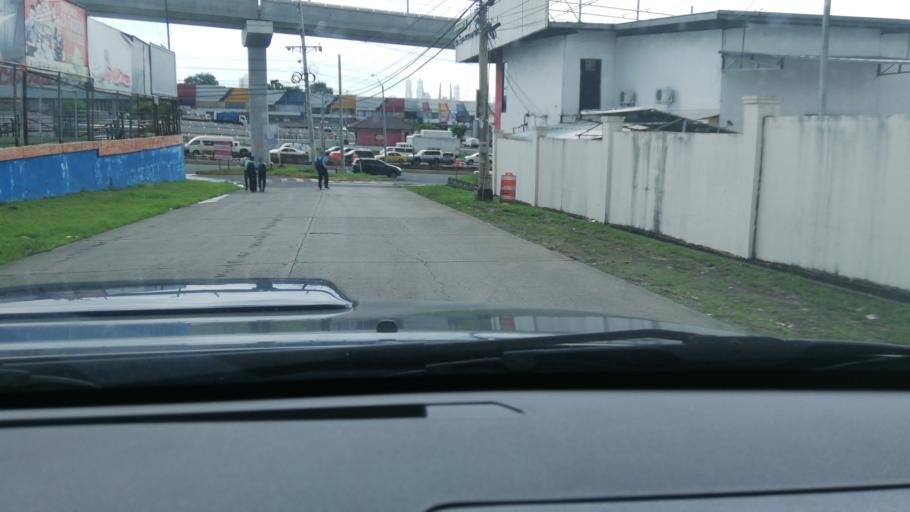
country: PA
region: Panama
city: San Miguelito
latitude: 9.0423
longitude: -79.4751
